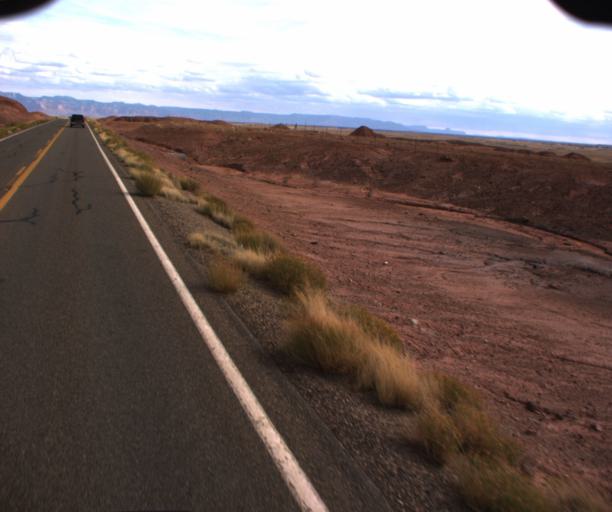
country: US
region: Arizona
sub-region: Apache County
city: Many Farms
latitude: 36.4680
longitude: -109.5494
